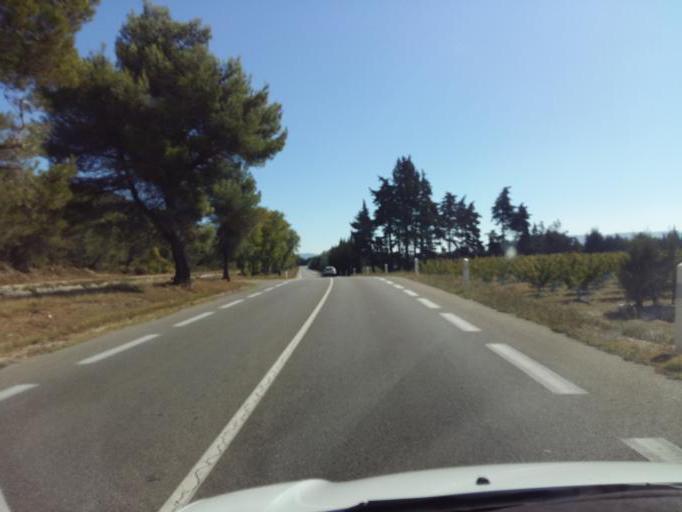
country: FR
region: Provence-Alpes-Cote d'Azur
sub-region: Departement des Bouches-du-Rhone
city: Senas
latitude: 43.7645
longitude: 5.1283
